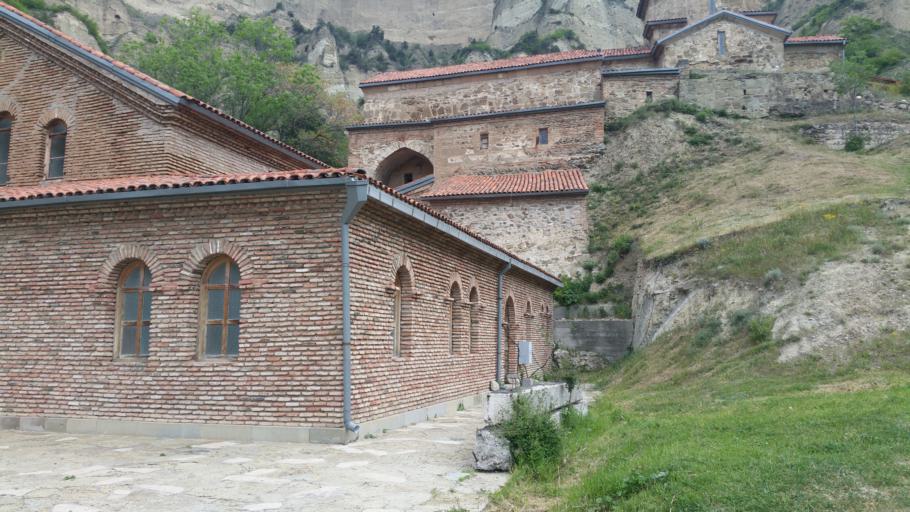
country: GE
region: Mtskheta-Mtianeti
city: Mtskheta
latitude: 41.8619
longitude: 44.6401
